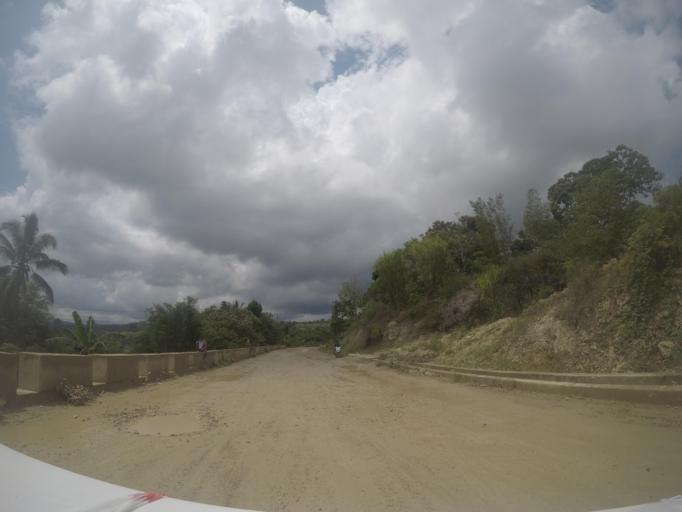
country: TL
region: Baucau
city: Venilale
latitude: -8.5848
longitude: 126.3893
